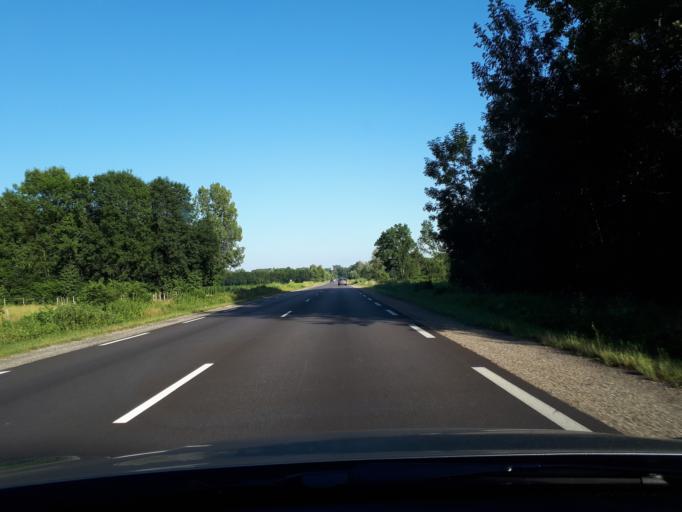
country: FR
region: Rhone-Alpes
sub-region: Departement de l'Isere
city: La Verpilliere
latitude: 45.6450
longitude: 5.1463
